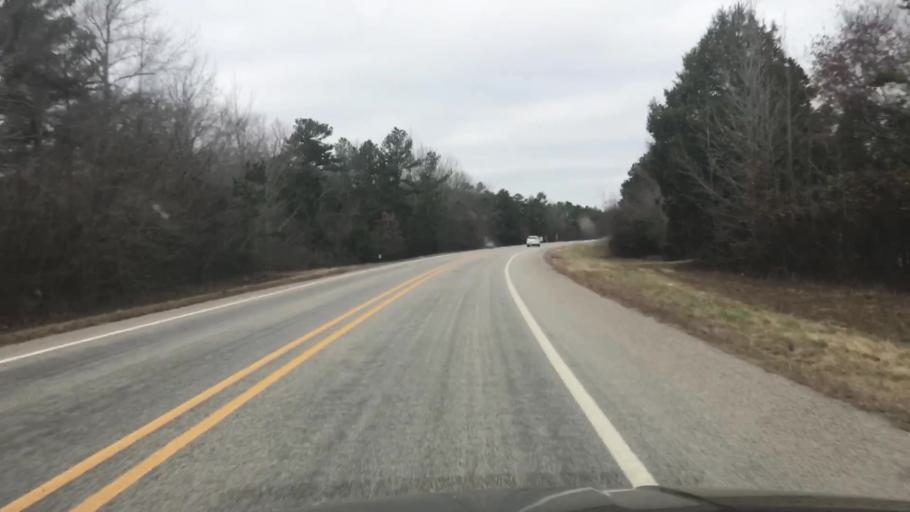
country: US
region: Arkansas
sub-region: Scott County
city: Waldron
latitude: 34.7045
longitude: -93.9277
